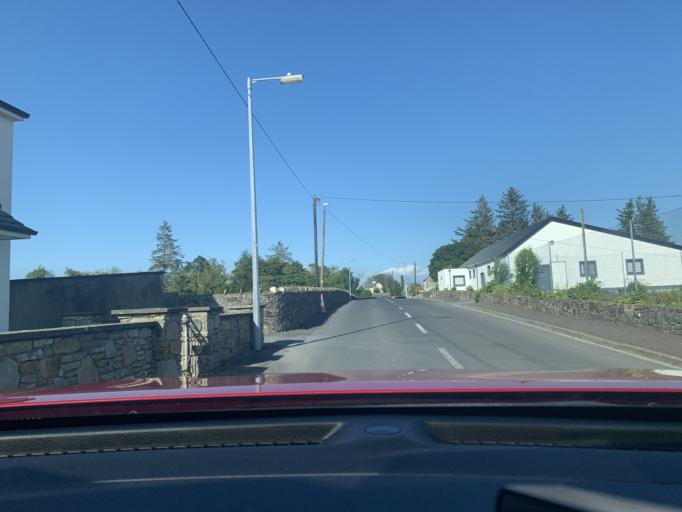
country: IE
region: Connaught
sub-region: Sligo
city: Tobercurry
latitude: 54.1008
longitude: -8.7778
